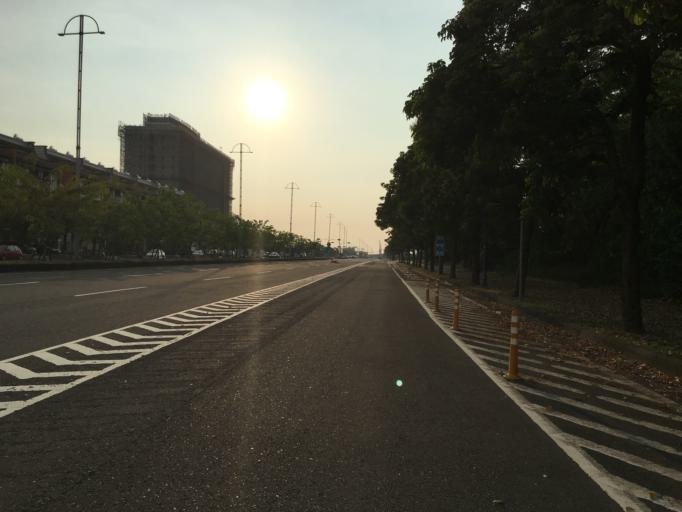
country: TW
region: Taiwan
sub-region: Chiayi
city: Taibao
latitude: 23.4690
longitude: 120.2976
